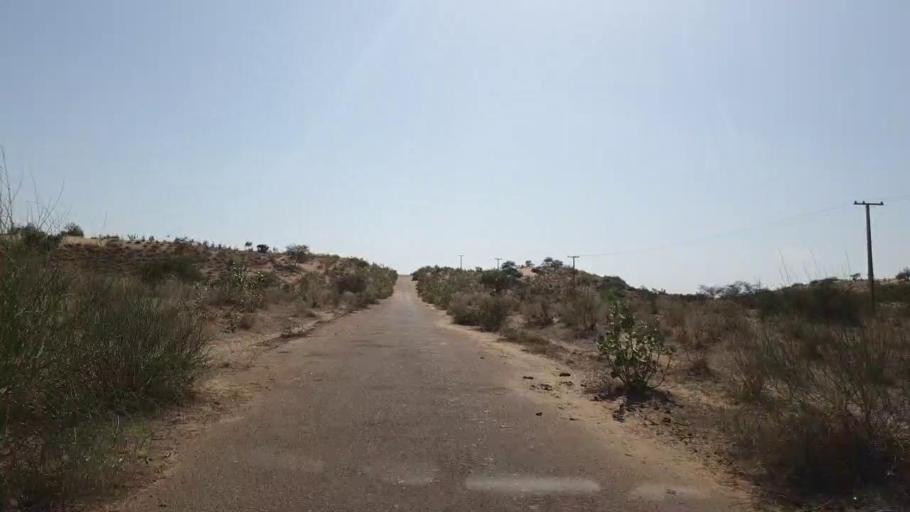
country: PK
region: Sindh
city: Umarkot
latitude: 25.1638
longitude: 70.0411
